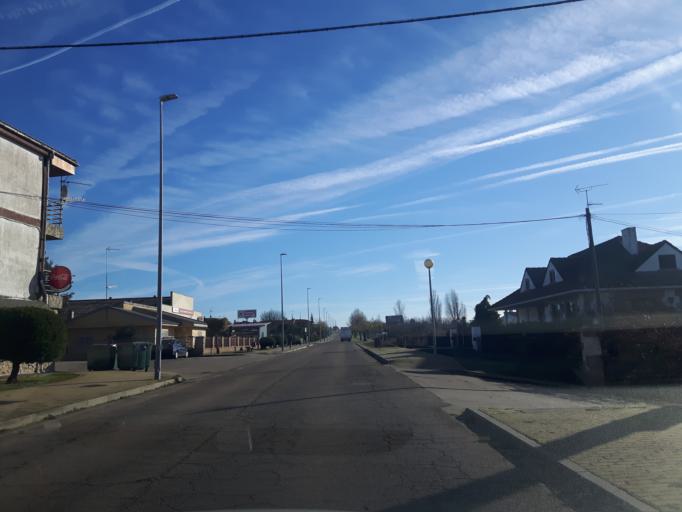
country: ES
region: Castille and Leon
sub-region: Provincia de Salamanca
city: Vitigudino
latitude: 41.0088
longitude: -6.4277
